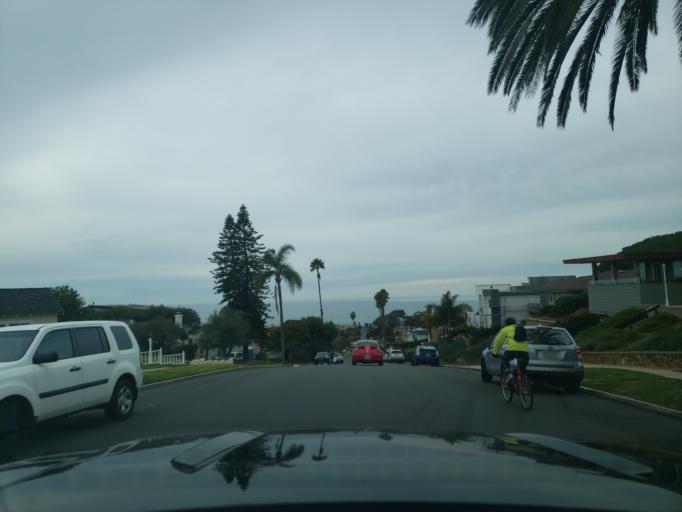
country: US
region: California
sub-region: San Diego County
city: Coronado
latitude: 32.7357
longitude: -117.2455
